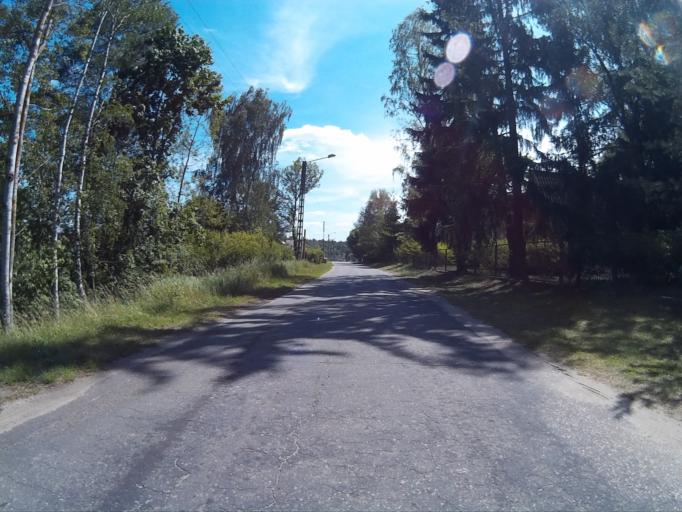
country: PL
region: Kujawsko-Pomorskie
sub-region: Powiat tucholski
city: Cekcyn
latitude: 53.6796
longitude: 17.9726
